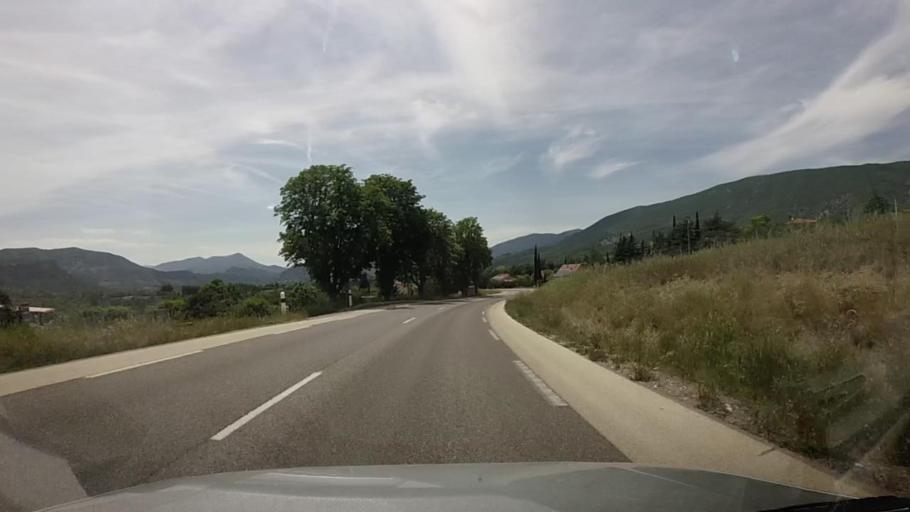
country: FR
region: Provence-Alpes-Cote d'Azur
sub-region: Departement des Alpes-de-Haute-Provence
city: Le Brusquet
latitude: 44.1593
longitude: 6.3035
